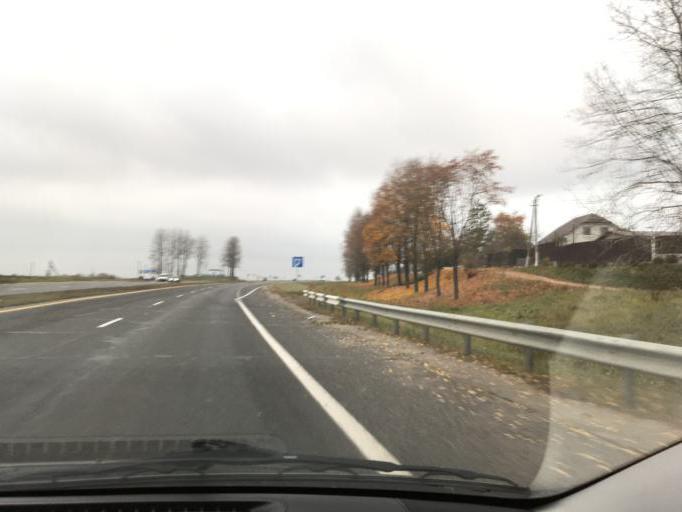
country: BY
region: Vitebsk
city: Vitebsk
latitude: 55.1514
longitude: 30.1142
